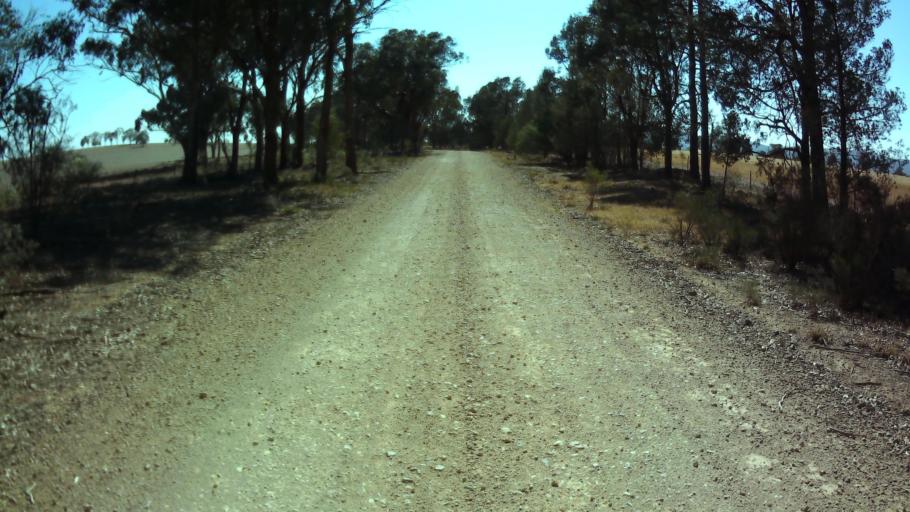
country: AU
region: New South Wales
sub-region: Weddin
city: Grenfell
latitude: -33.9036
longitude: 147.8620
